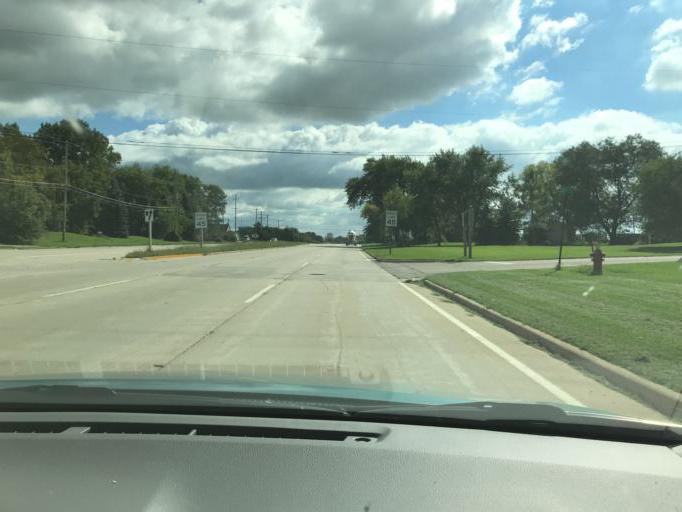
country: US
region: Wisconsin
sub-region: Kenosha County
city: Pleasant Prairie
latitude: 42.5619
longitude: -87.8890
